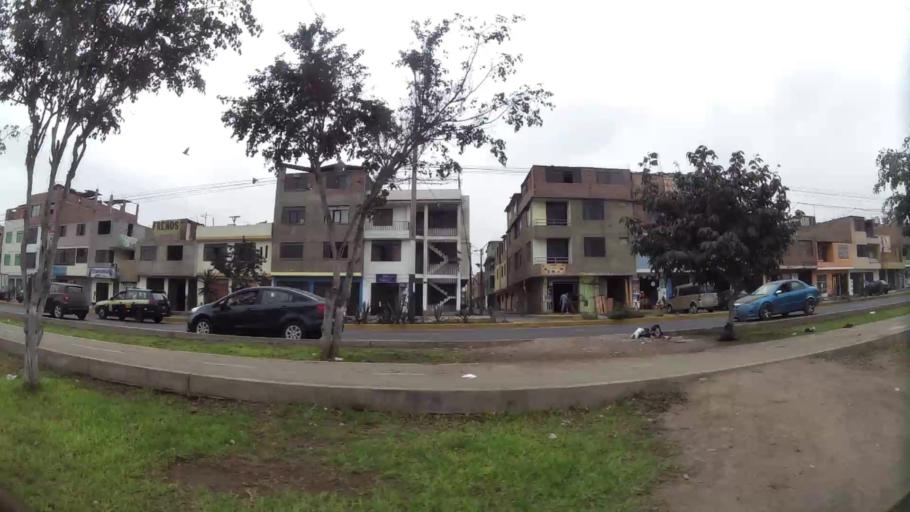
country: PE
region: Lima
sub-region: Lima
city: Independencia
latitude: -11.9835
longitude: -77.0764
